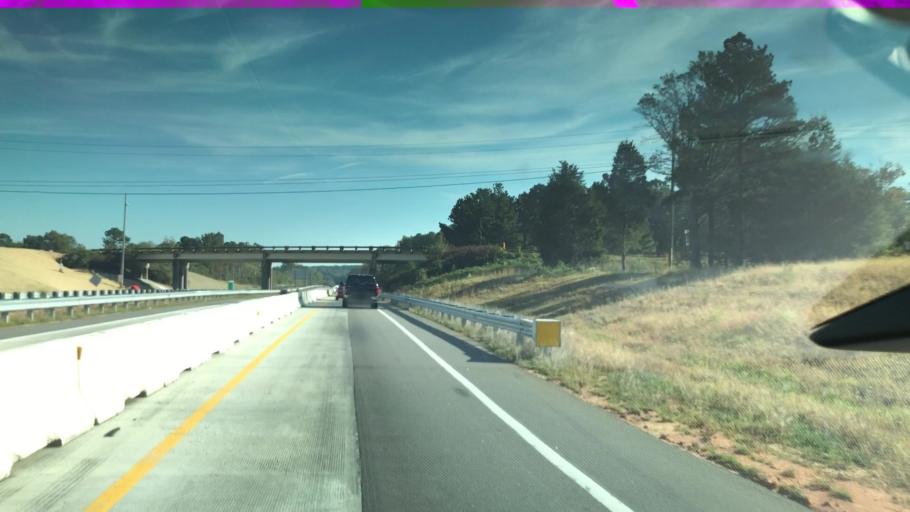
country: US
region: North Carolina
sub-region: Vance County
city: Henderson
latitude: 36.3609
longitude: -78.3756
